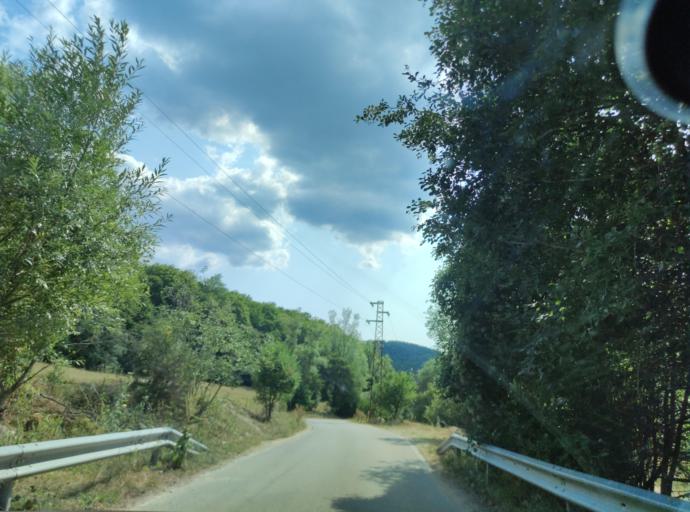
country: BG
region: Blagoevgrad
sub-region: Obshtina Belitsa
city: Belitsa
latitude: 42.0151
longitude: 23.5701
